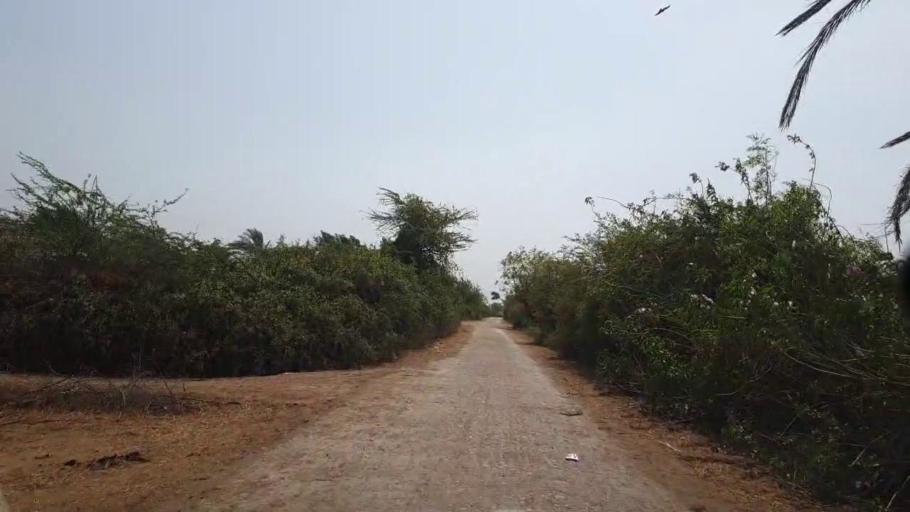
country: PK
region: Sindh
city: Matli
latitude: 25.0342
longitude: 68.7039
